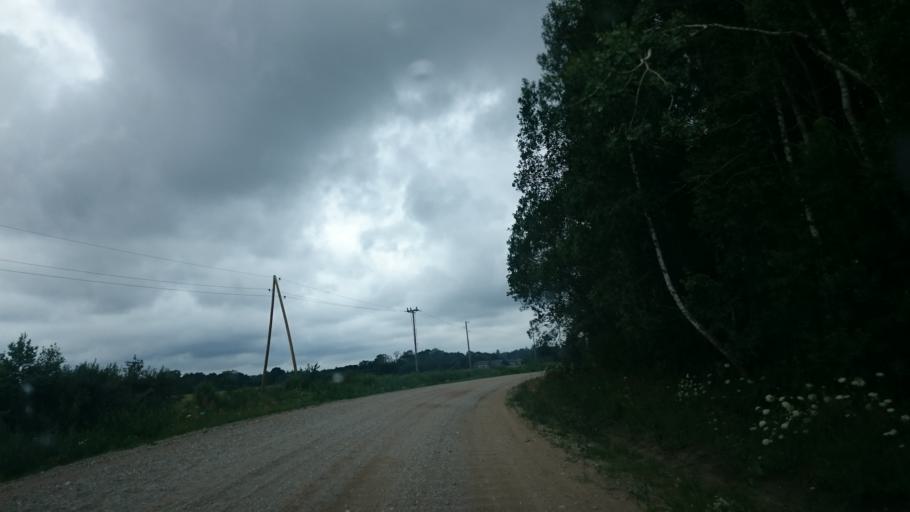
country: LV
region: Pavilostas
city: Pavilosta
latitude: 56.8523
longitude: 21.2498
